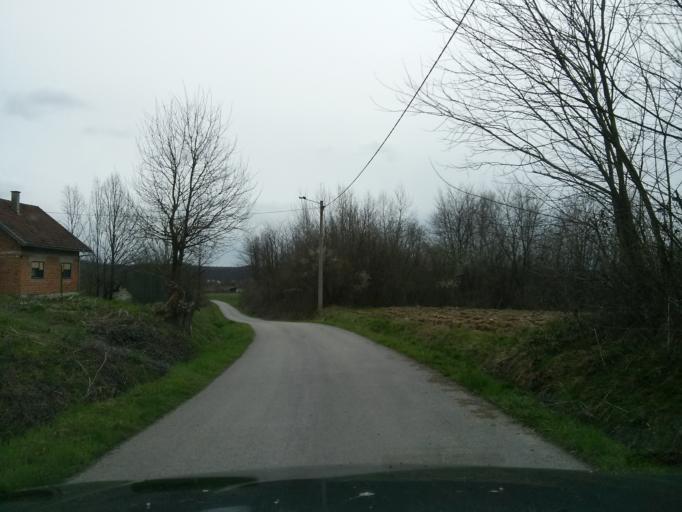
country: HR
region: Sisacko-Moslavacka
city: Gvozd
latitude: 45.2831
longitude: 15.9568
